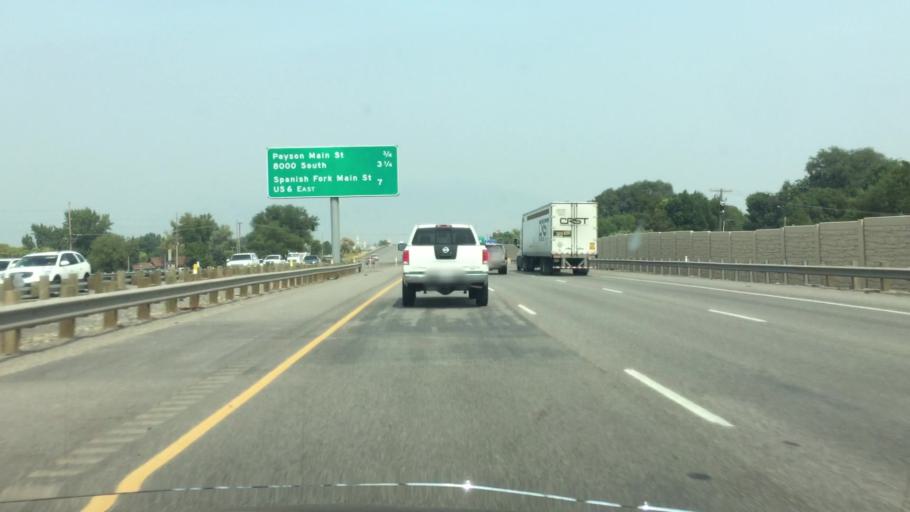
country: US
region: Utah
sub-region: Utah County
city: Payson
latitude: 40.0440
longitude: -111.7443
